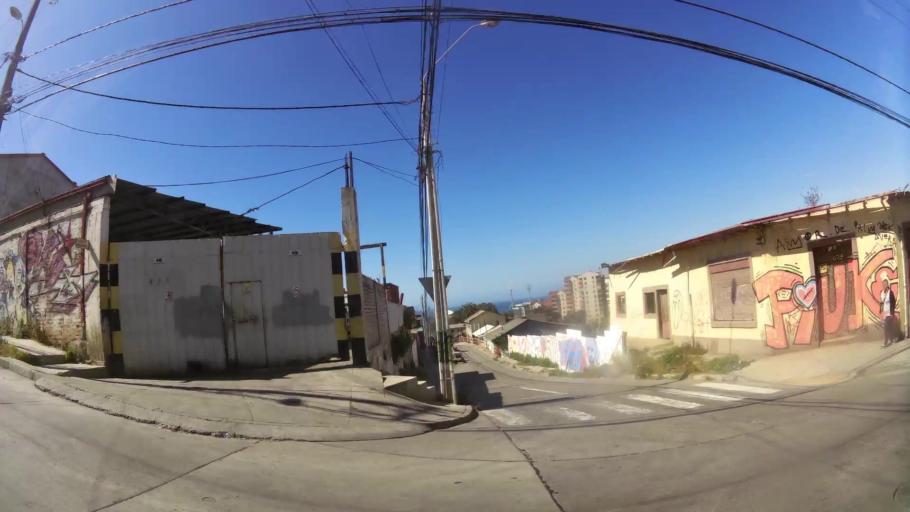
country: CL
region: Valparaiso
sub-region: Provincia de Valparaiso
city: Valparaiso
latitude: -33.0263
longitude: -71.6433
